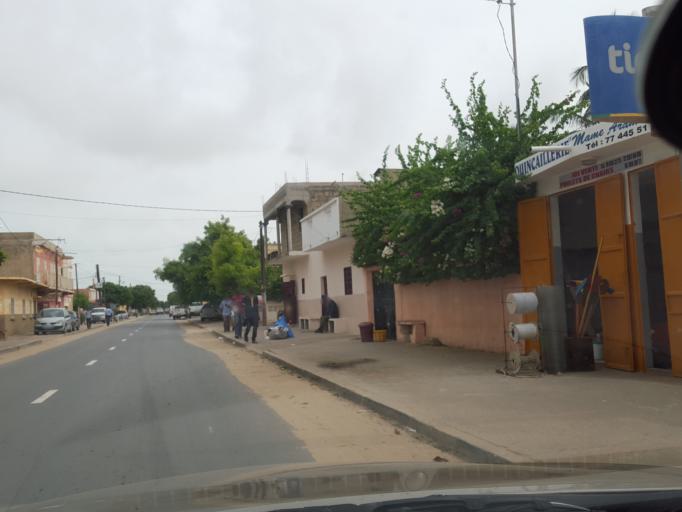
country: SN
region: Saint-Louis
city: Saint-Louis
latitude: 16.0276
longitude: -16.4890
